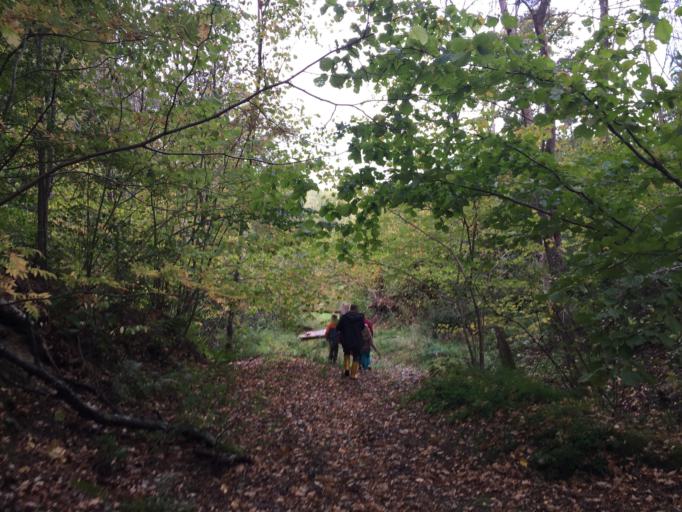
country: LV
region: Ligatne
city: Ligatne
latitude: 57.2130
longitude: 25.0650
